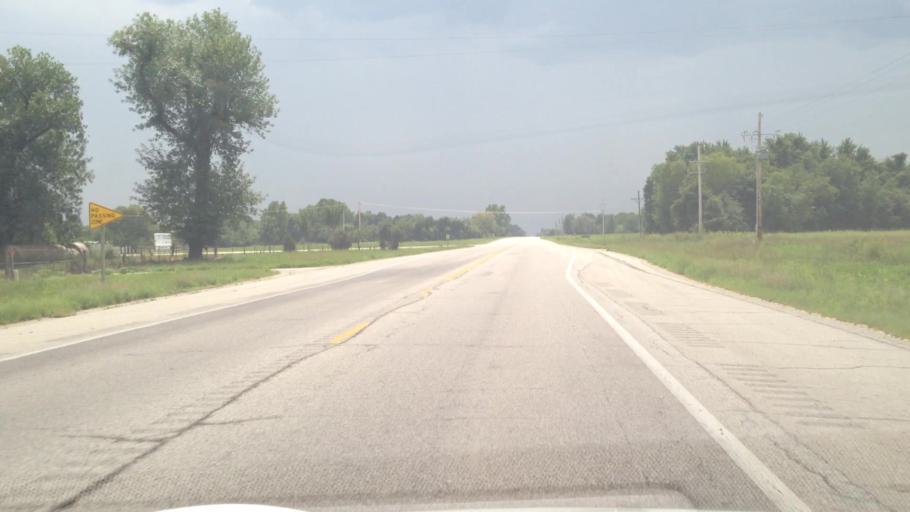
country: US
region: Kansas
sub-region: Cherokee County
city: Galena
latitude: 37.1232
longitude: -94.7044
